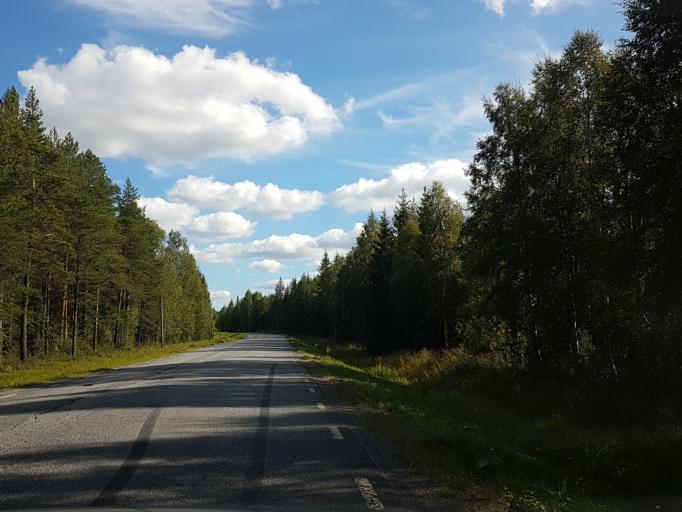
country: SE
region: Vaesterbotten
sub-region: Skelleftea Kommun
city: Burtraesk
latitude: 64.3279
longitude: 20.5259
